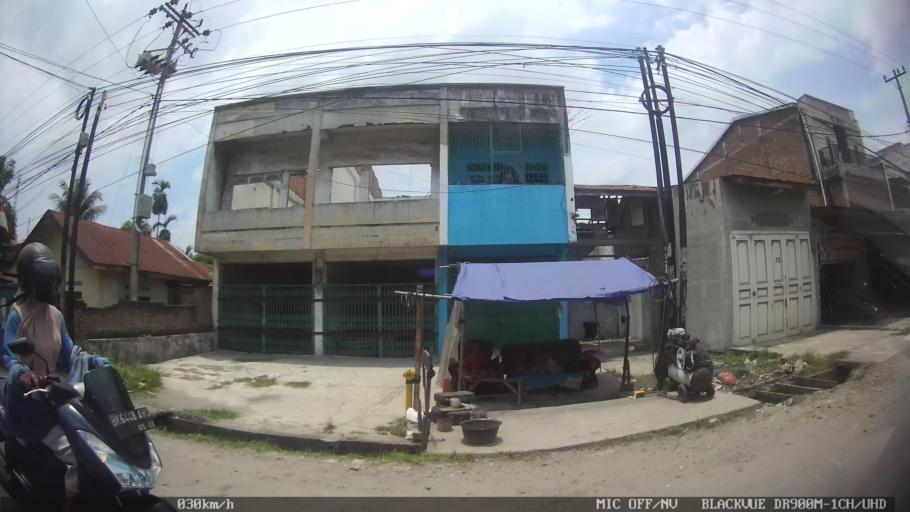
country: ID
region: North Sumatra
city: Labuhan Deli
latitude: 3.6861
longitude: 98.6665
